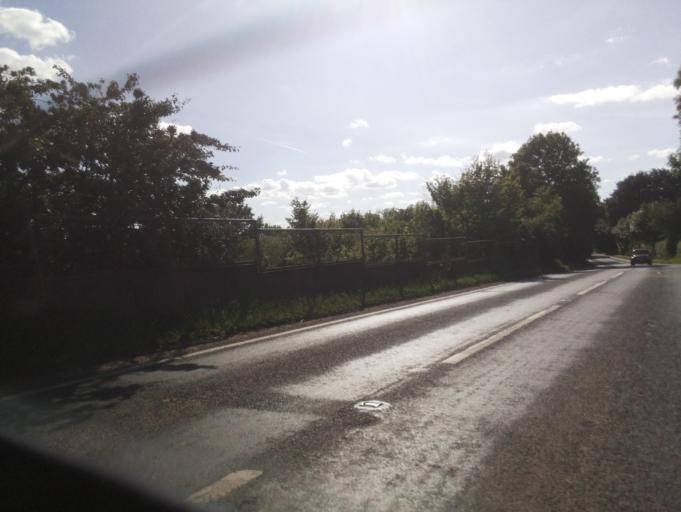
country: GB
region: England
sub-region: Somerset
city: North Petherton
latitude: 51.0480
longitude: -2.9919
